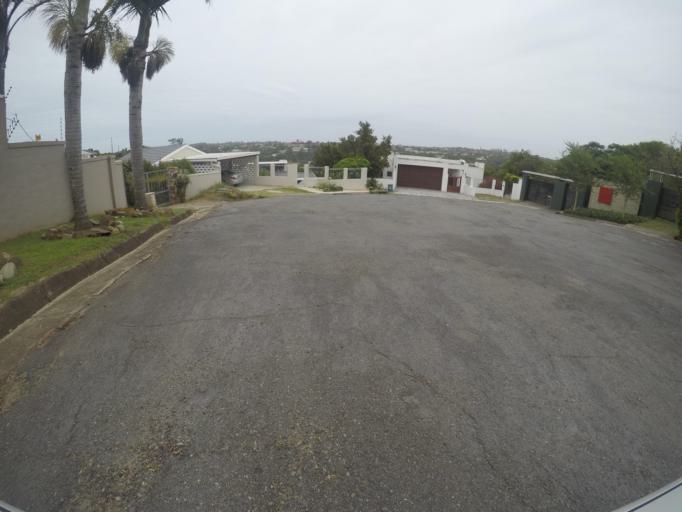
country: ZA
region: Eastern Cape
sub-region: Buffalo City Metropolitan Municipality
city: East London
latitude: -32.9756
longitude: 27.9353
